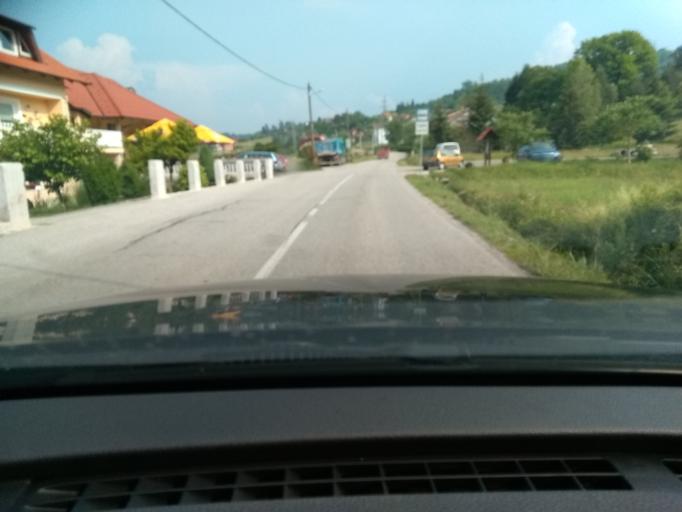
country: HR
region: Krapinsko-Zagorska
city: Pregrada
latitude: 46.0687
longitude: 15.7635
